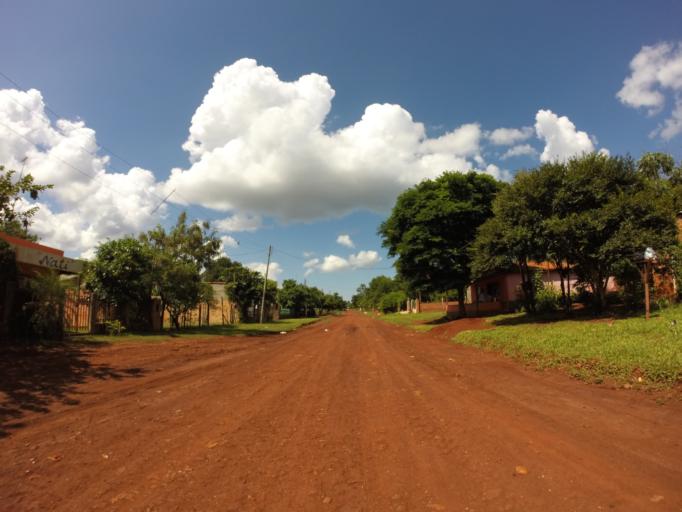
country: PY
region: Alto Parana
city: Ciudad del Este
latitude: -25.3731
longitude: -54.6516
